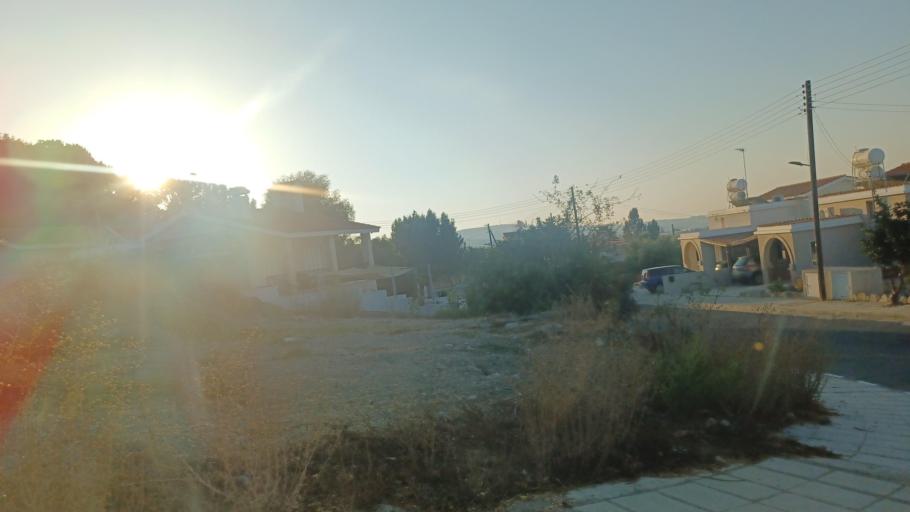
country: CY
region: Pafos
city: Mesogi
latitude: 34.8141
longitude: 32.4414
